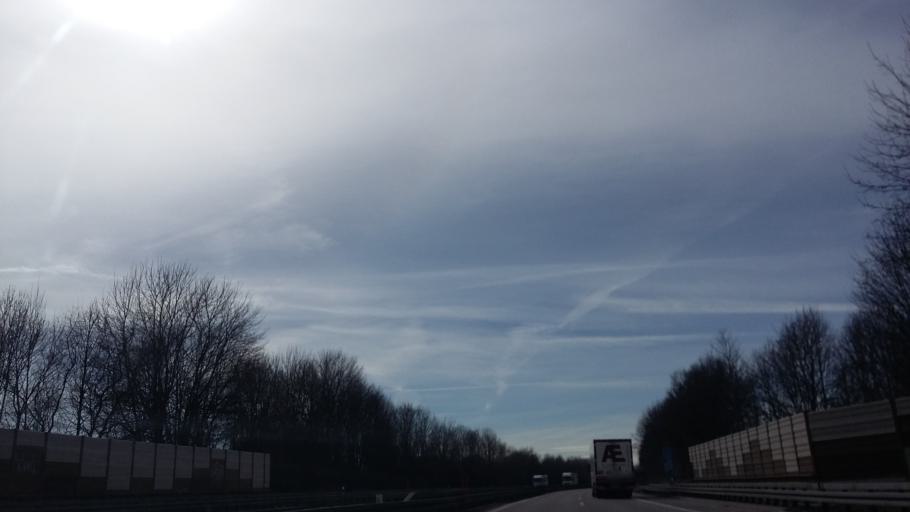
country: DE
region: Baden-Wuerttemberg
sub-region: Tuebingen Region
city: Aitrach
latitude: 47.9380
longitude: 10.0986
